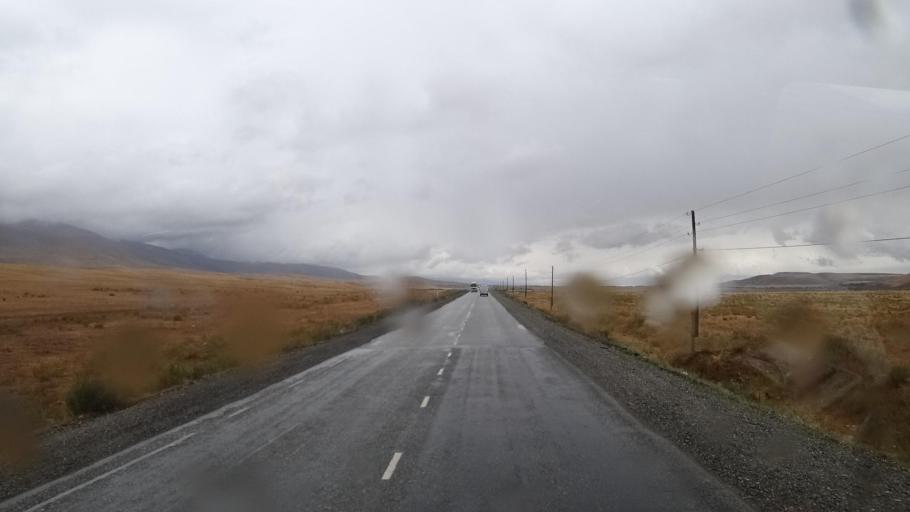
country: KG
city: Sosnovka
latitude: 42.2215
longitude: 73.7025
